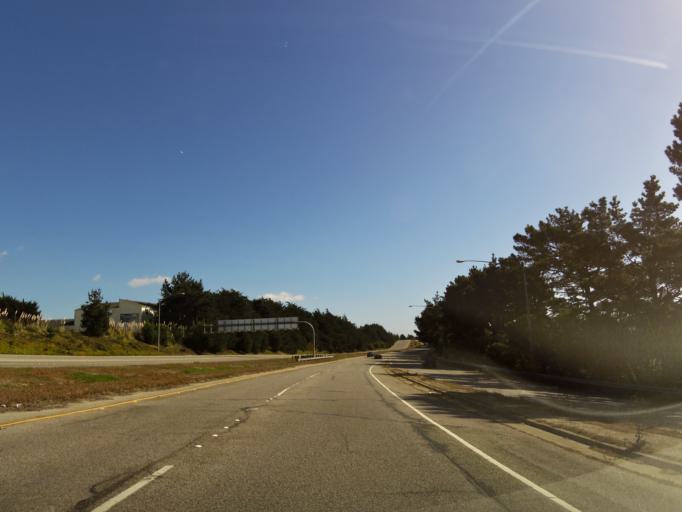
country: US
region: California
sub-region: San Mateo County
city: Broadmoor
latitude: 37.6667
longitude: -122.4824
